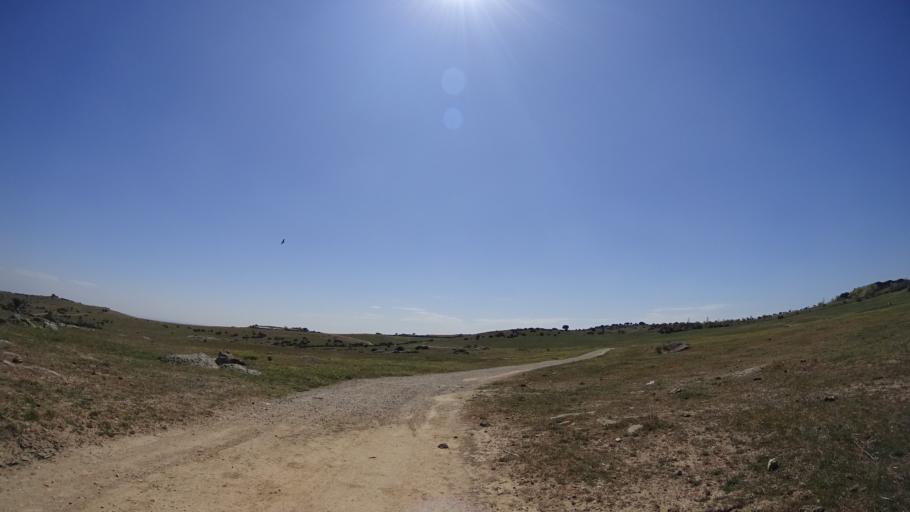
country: ES
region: Madrid
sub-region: Provincia de Madrid
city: Colmenar Viejo
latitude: 40.6966
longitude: -3.7564
